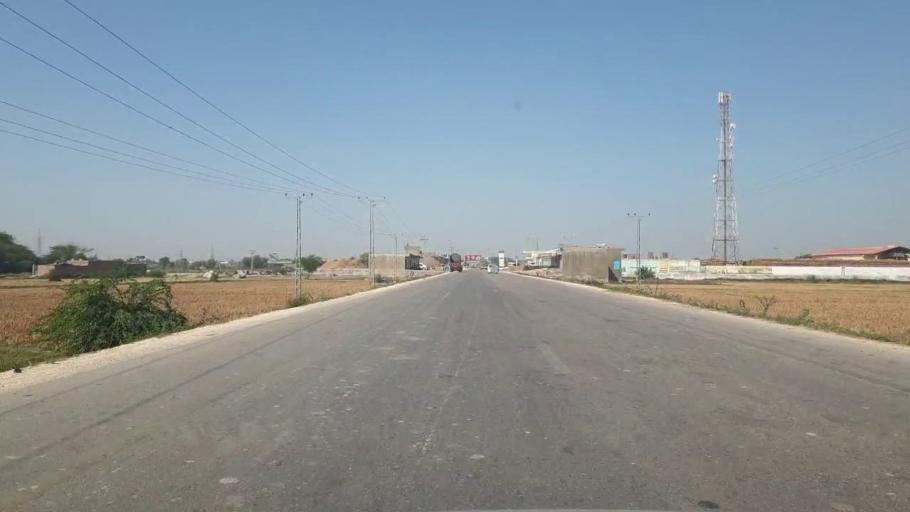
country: PK
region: Sindh
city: Talhar
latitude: 24.8805
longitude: 68.8117
